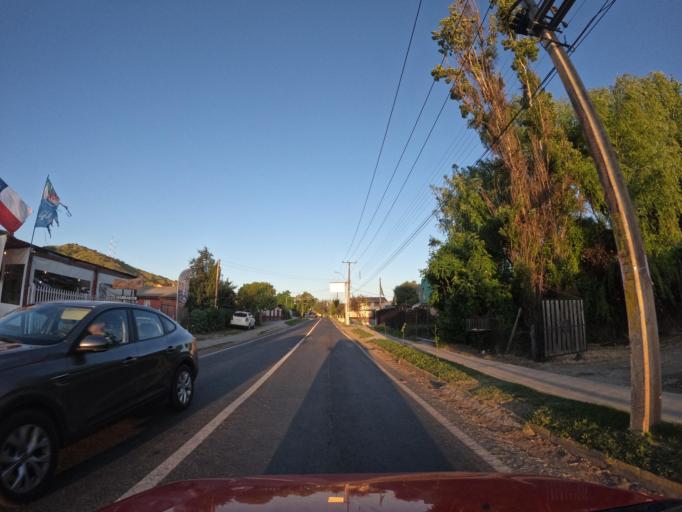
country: CL
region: Maule
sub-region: Provincia de Talca
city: Talca
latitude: -35.0902
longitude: -71.6547
